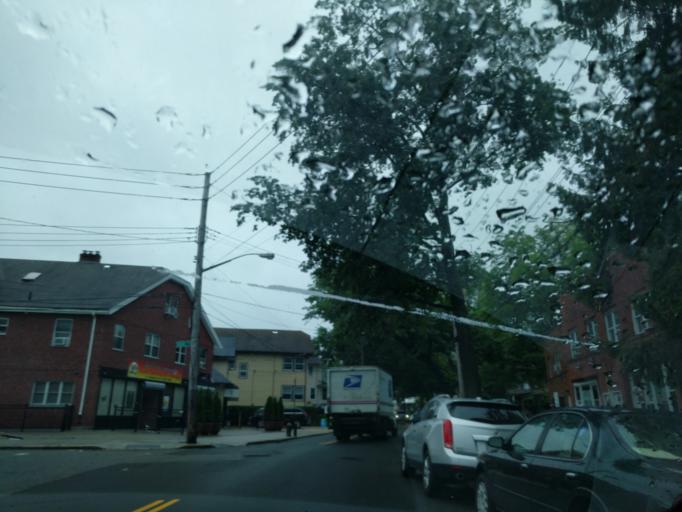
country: US
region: New Jersey
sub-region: Hudson County
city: Bayonne
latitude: 40.6189
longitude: -74.1234
